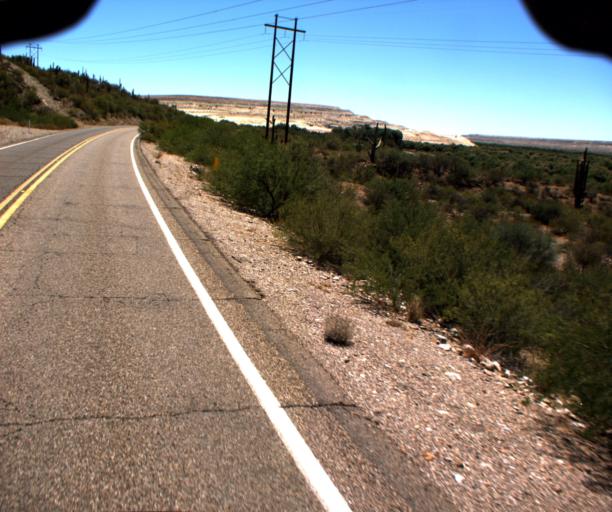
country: US
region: Arizona
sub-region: Pinal County
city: Kearny
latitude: 33.0140
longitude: -110.8282
